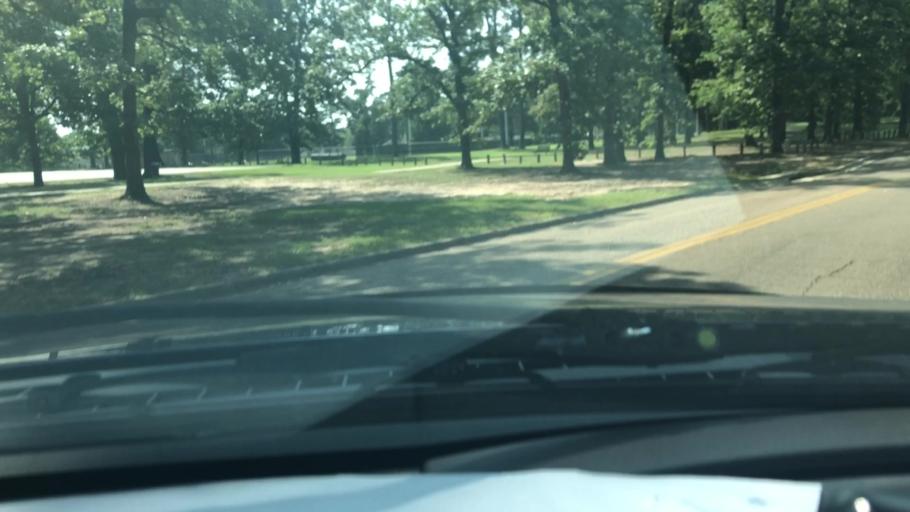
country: US
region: Arkansas
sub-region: Miller County
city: Texarkana
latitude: 33.4607
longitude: -94.0583
